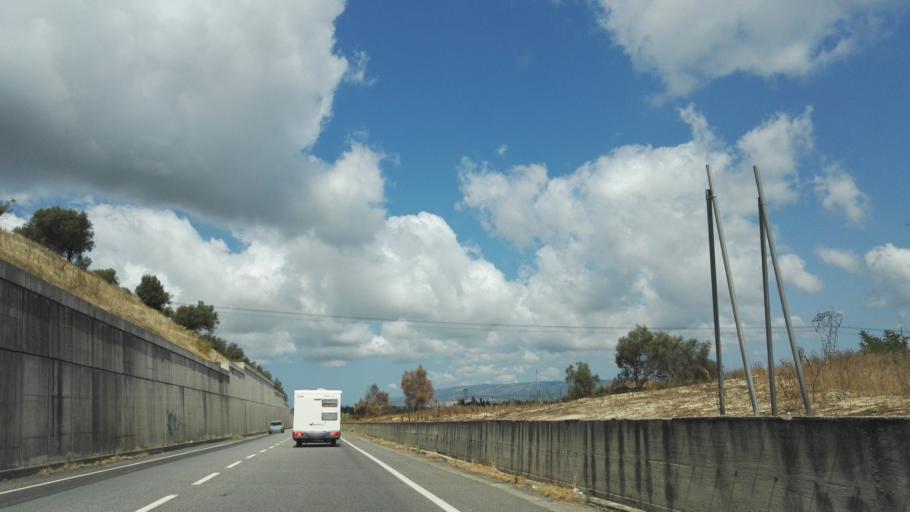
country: IT
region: Calabria
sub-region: Provincia di Reggio Calabria
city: Rosarno
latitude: 38.4619
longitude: 16.0160
